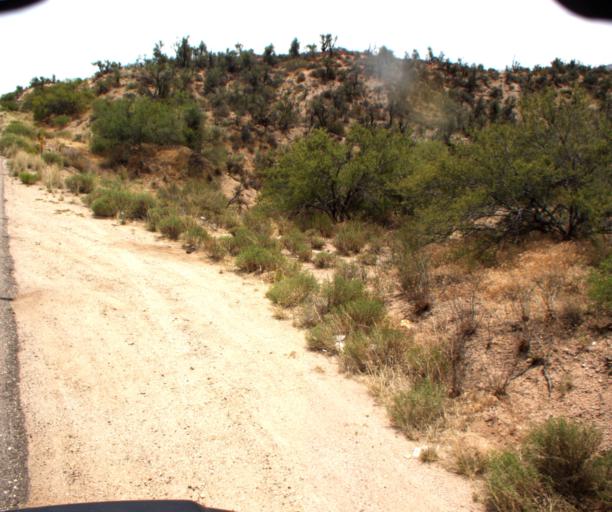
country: US
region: Arizona
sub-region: Gila County
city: San Carlos
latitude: 33.3396
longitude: -110.5978
